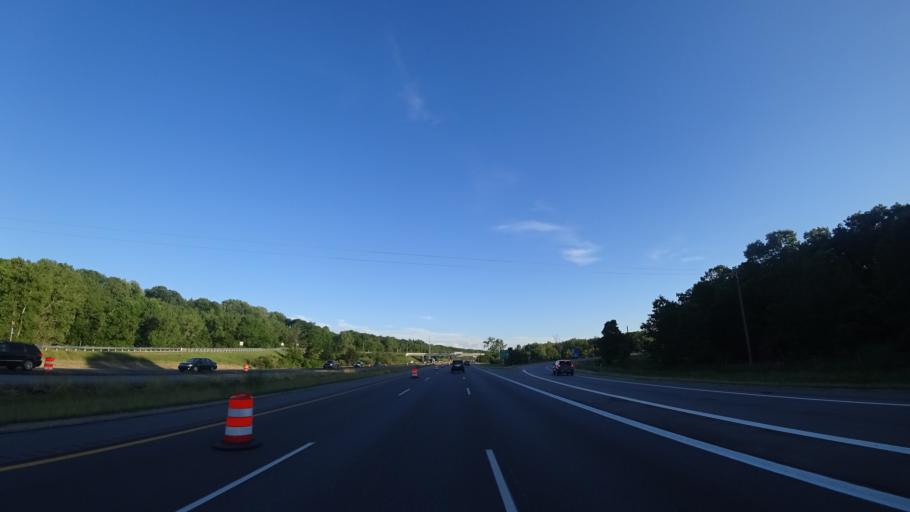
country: US
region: Michigan
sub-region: Berrien County
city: Stevensville
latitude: 42.0136
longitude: -86.5327
